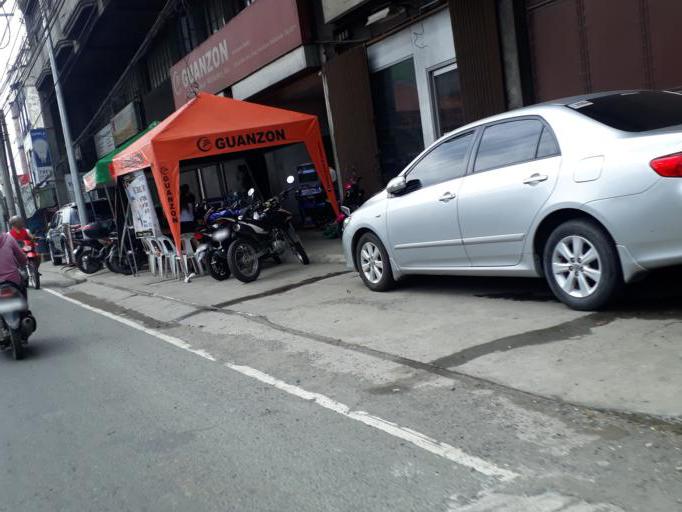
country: PH
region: Calabarzon
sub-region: Province of Rizal
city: Valenzuela
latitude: 14.6844
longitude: 120.9771
